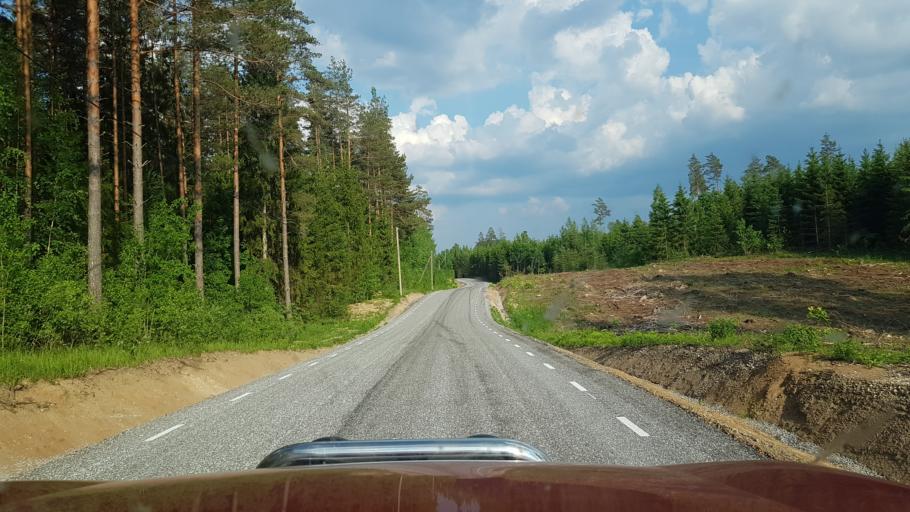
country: EE
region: Tartu
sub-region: UElenurme vald
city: Ulenurme
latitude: 58.1091
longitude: 26.7455
